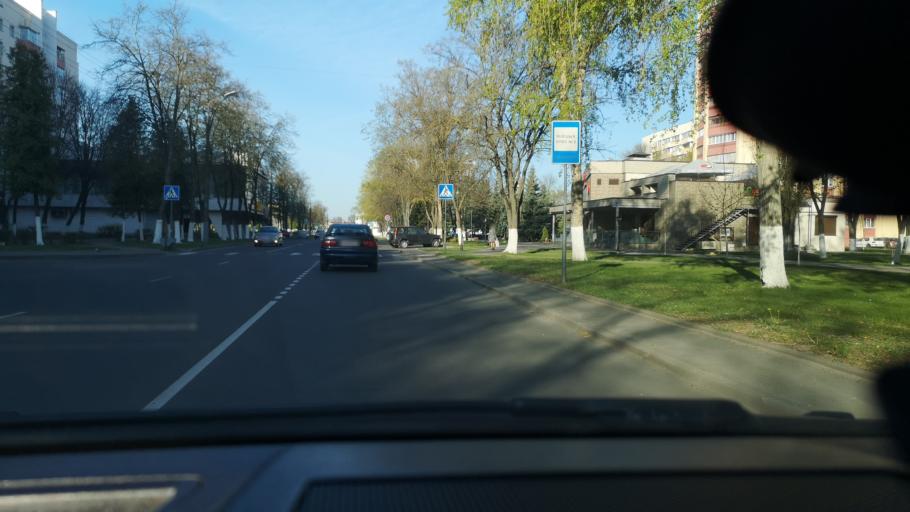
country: BY
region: Gomel
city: Gomel
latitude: 52.4511
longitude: 31.0001
